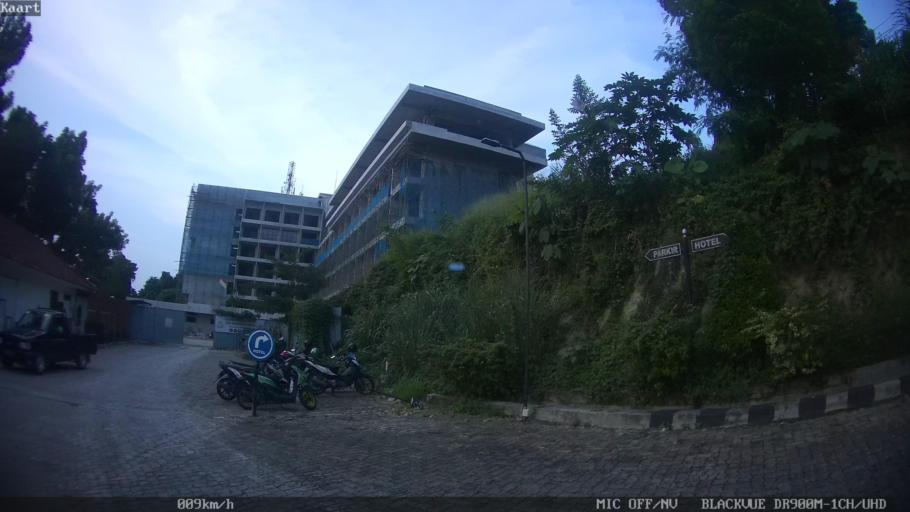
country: ID
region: Lampung
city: Bandarlampung
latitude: -5.4108
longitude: 105.2628
